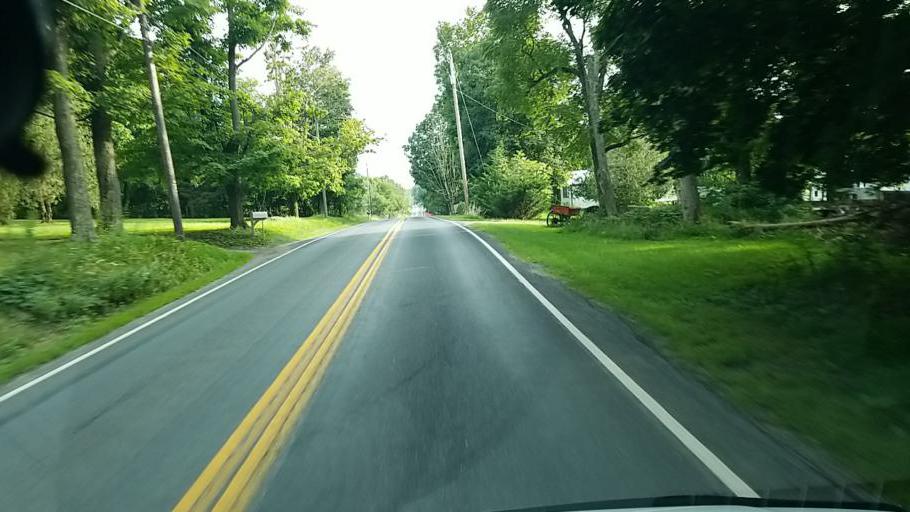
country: US
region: Pennsylvania
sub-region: Cumberland County
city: Newville
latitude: 40.2558
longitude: -77.4418
